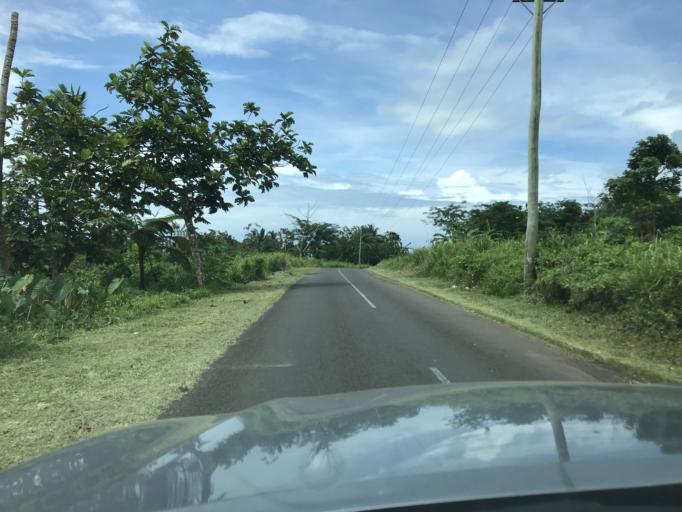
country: WS
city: Fasito`outa
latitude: -13.8626
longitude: -171.9105
